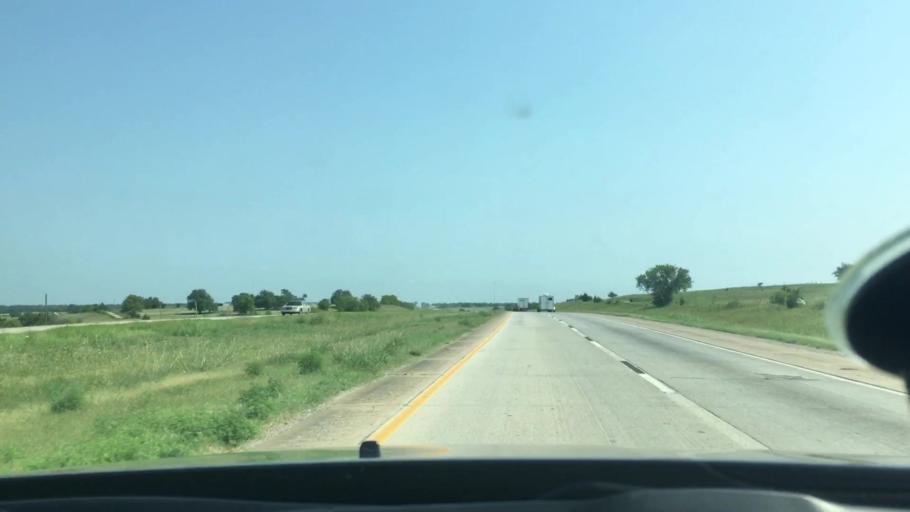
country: US
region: Oklahoma
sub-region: Bryan County
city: Durant
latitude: 34.1380
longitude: -96.2694
